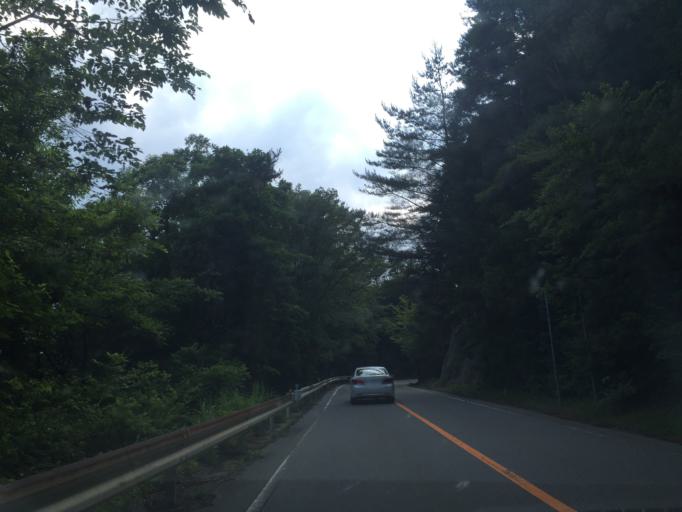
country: JP
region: Aichi
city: Shinshiro
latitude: 35.1828
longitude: 137.6134
